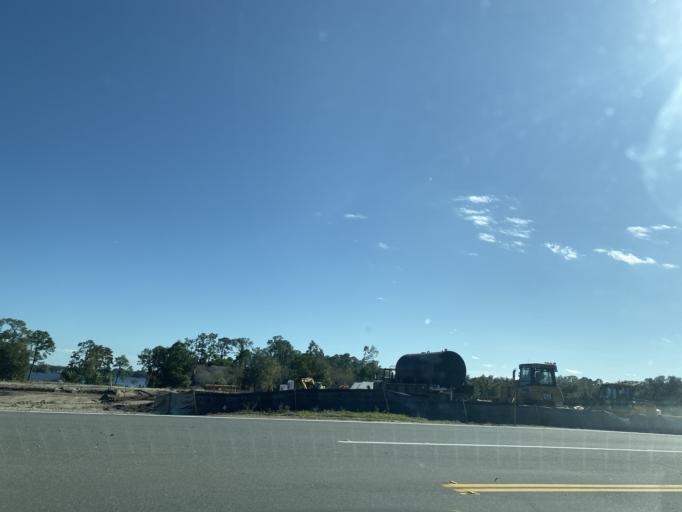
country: US
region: Florida
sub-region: Orange County
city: Meadow Woods
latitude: 28.3983
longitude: -81.2423
